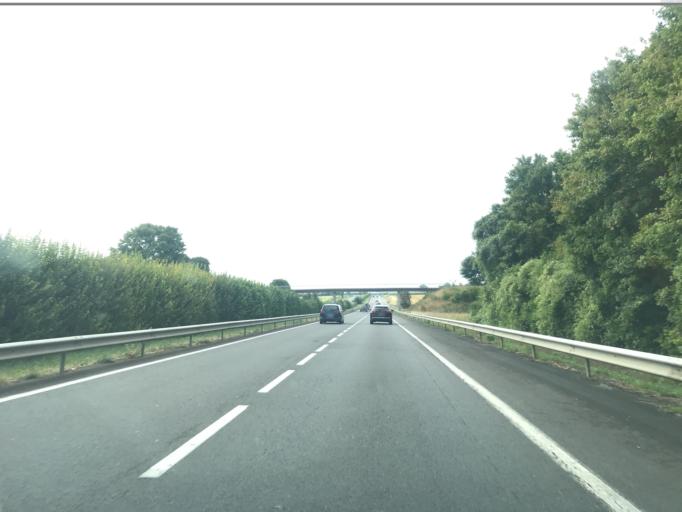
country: FR
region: Poitou-Charentes
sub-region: Departement de la Vienne
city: Chaunay
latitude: 46.1727
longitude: 0.1675
